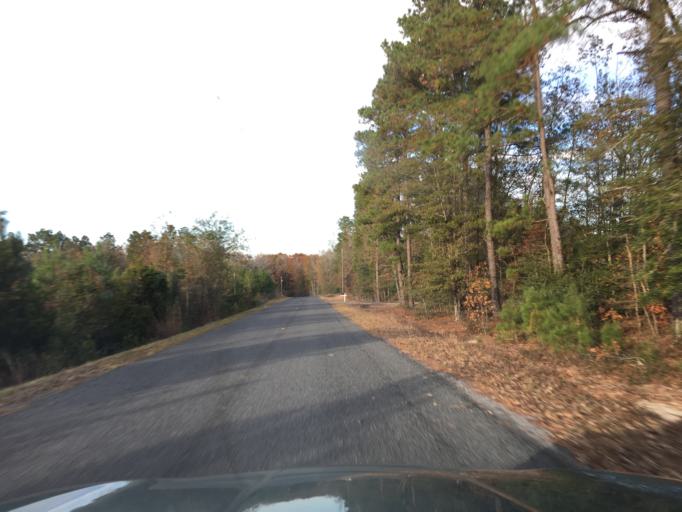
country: US
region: South Carolina
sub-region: Barnwell County
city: Williston
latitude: 33.6701
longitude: -81.3715
